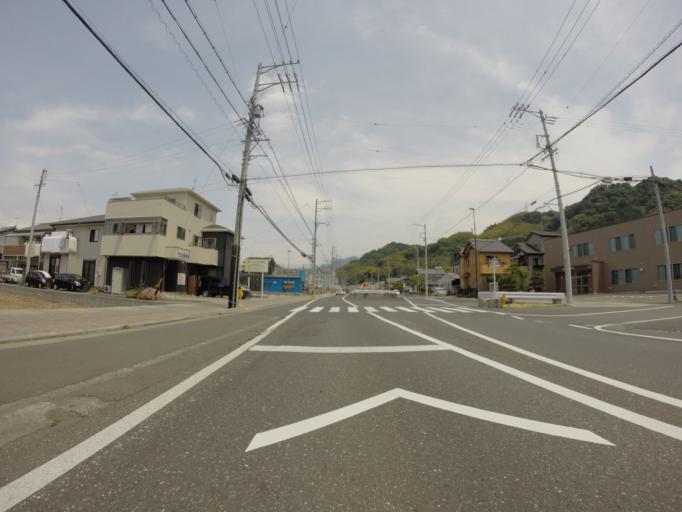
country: JP
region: Shizuoka
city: Shizuoka-shi
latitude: 35.0125
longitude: 138.3745
